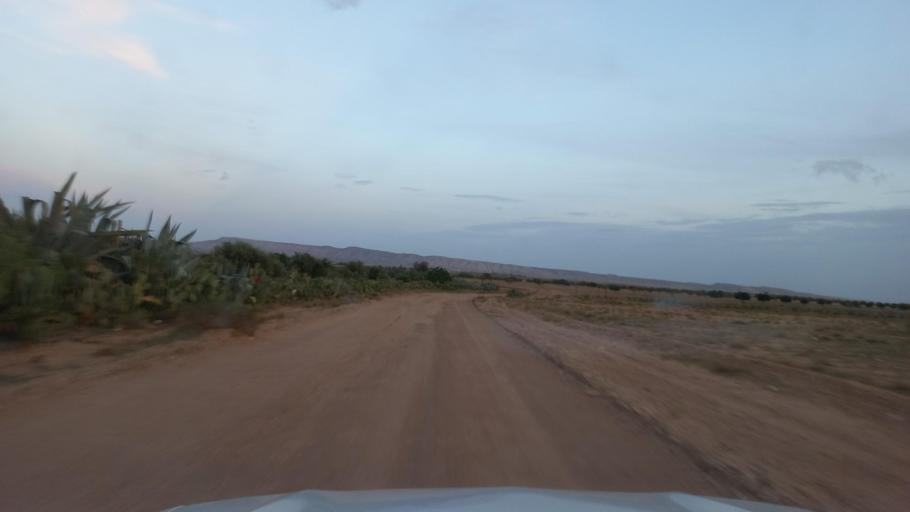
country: TN
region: Al Qasrayn
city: Sbiba
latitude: 35.3497
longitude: 9.0443
